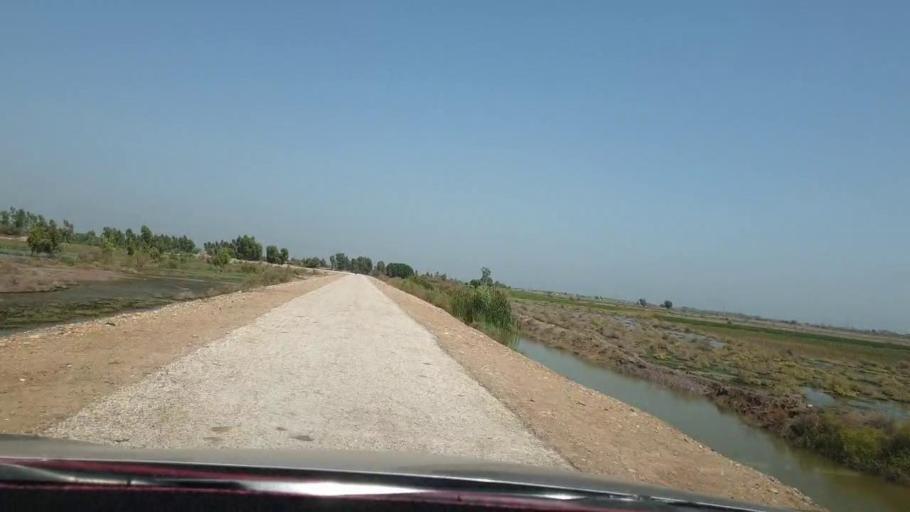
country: PK
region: Sindh
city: Warah
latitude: 27.5356
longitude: 67.7333
